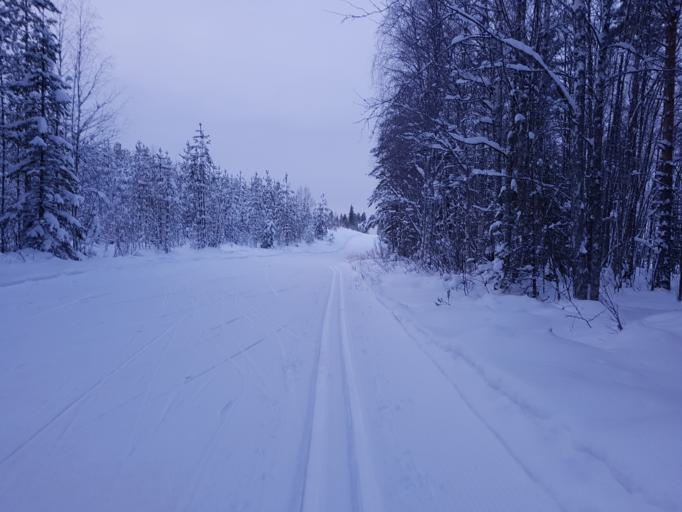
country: FI
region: Kainuu
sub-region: Kehys-Kainuu
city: Kuhmo
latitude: 64.1135
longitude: 29.5651
